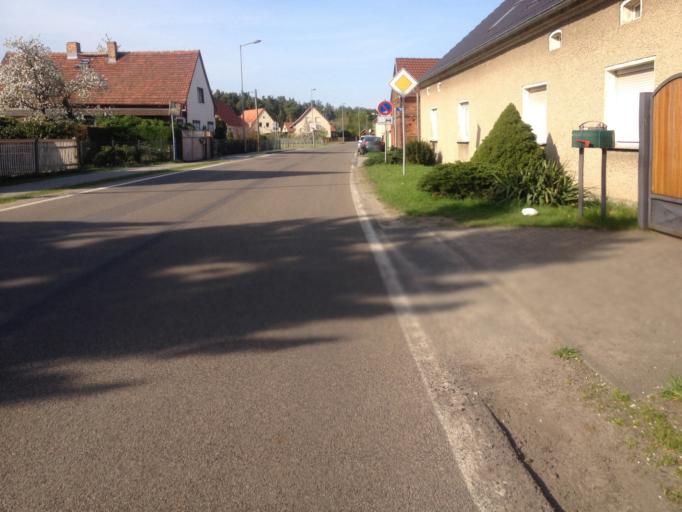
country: DE
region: Brandenburg
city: Briesen
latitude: 51.8536
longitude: 14.2487
